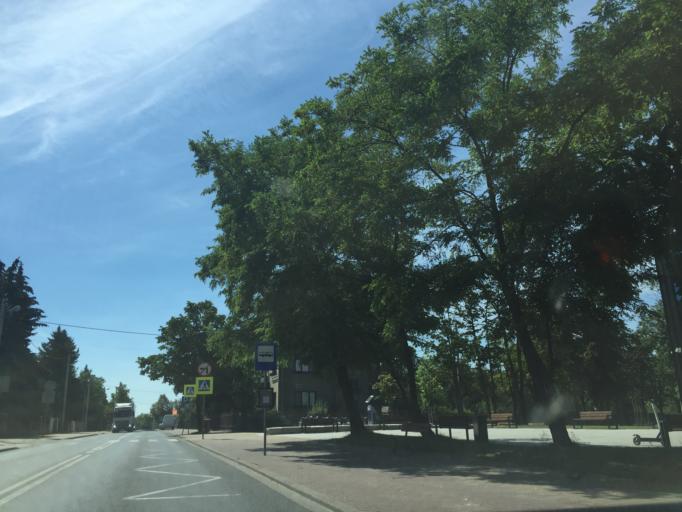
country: PL
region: Lodz Voivodeship
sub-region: Piotrkow Trybunalski
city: Piotrkow Trybunalski
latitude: 51.4086
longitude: 19.7038
